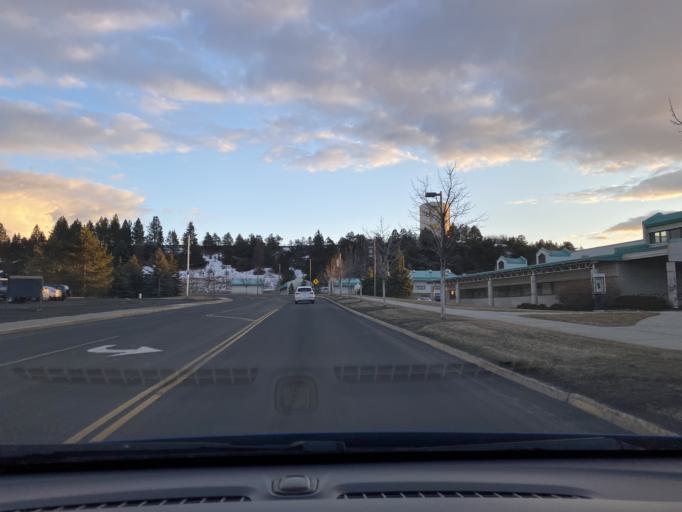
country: US
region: Idaho
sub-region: Latah County
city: Moscow
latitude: 46.7278
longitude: -117.0233
